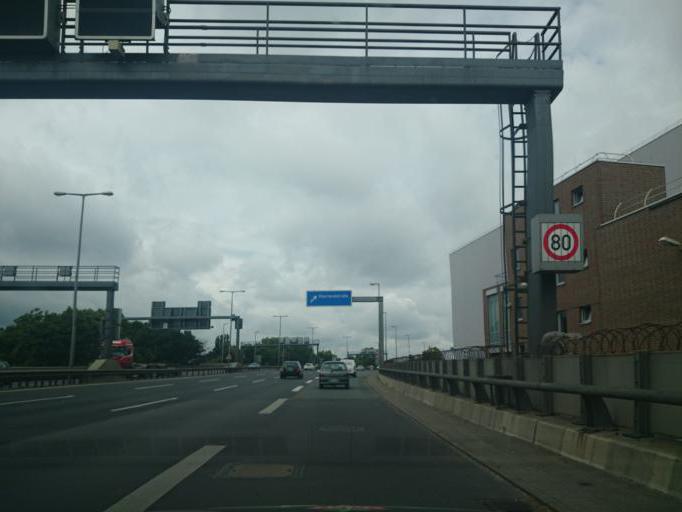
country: DE
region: Berlin
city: Tempelhof Bezirk
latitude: 52.4619
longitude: 13.4077
